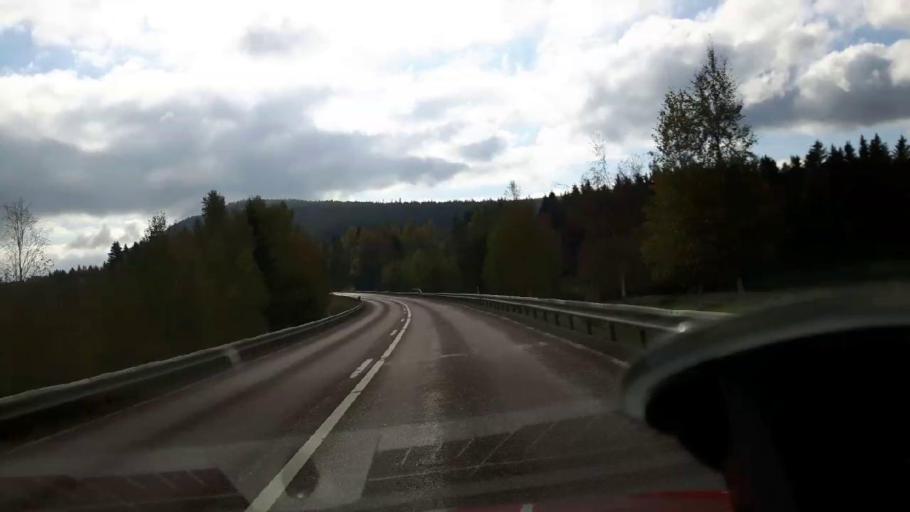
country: SE
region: Gaevleborg
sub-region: Bollnas Kommun
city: Arbra
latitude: 61.5781
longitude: 16.3164
